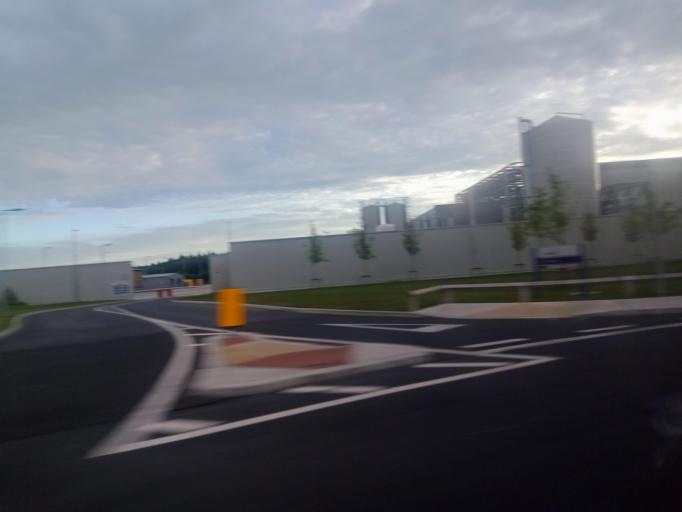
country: IE
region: Leinster
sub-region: Laois
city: Portlaoise
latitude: 53.0168
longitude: -7.3152
